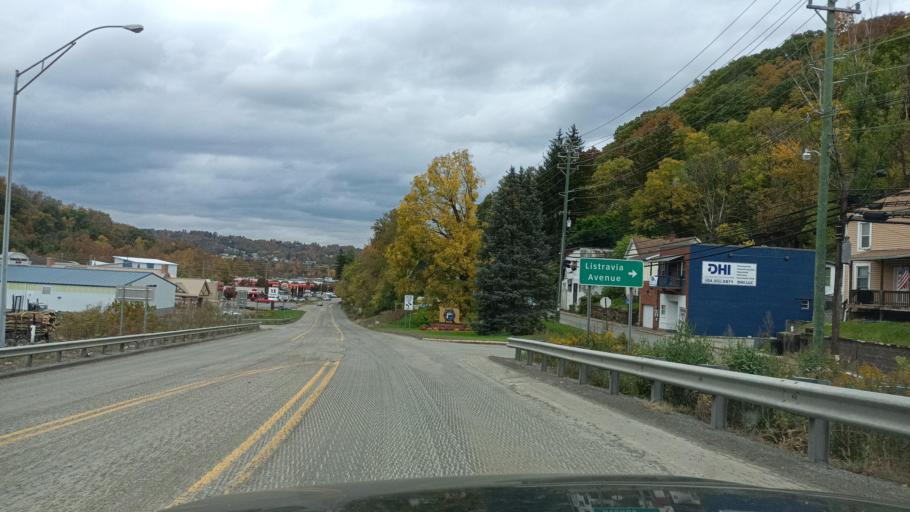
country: US
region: West Virginia
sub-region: Monongalia County
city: Brookhaven
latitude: 39.6167
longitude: -79.9213
